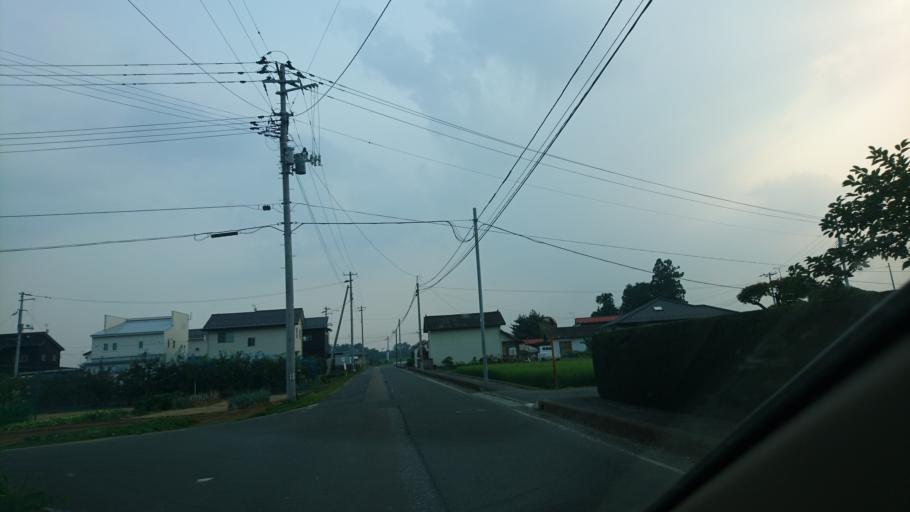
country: JP
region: Iwate
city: Mizusawa
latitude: 39.1705
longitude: 141.1687
